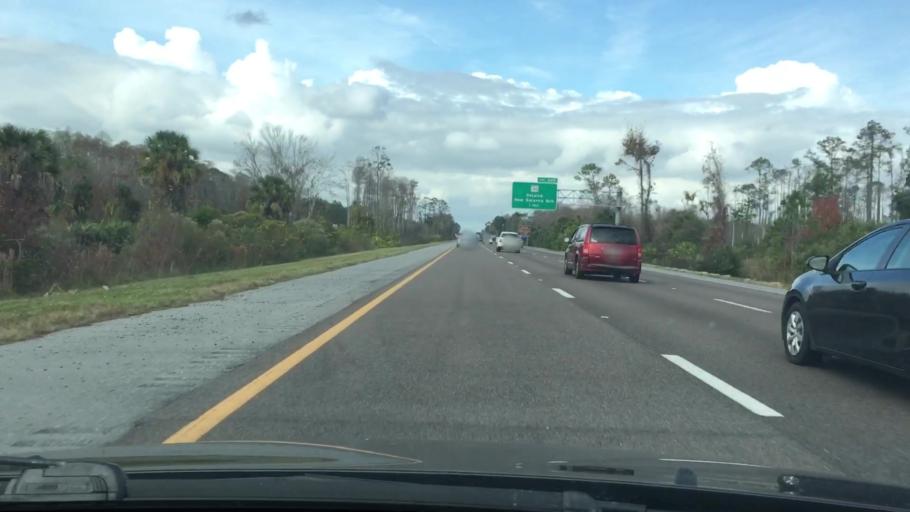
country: US
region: Florida
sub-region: Volusia County
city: Glencoe
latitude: 28.9959
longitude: -80.9766
